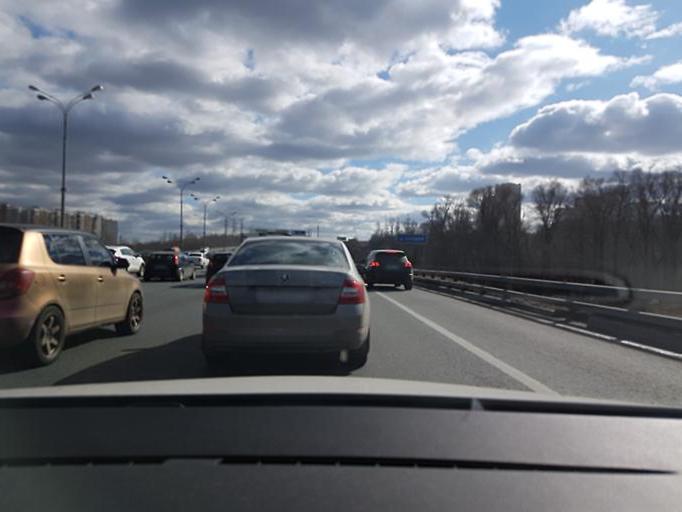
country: RU
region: Moscow
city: Strogino
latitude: 55.8440
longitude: 37.3923
